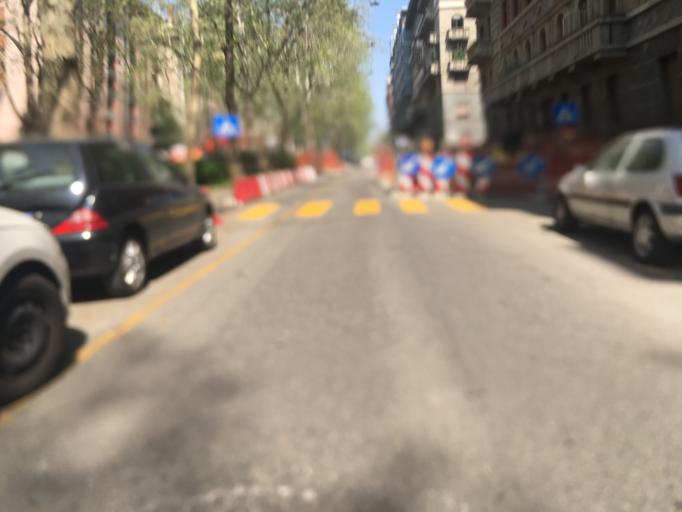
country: IT
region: Lombardy
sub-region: Citta metropolitana di Milano
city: Milano
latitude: 45.4722
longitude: 9.1481
